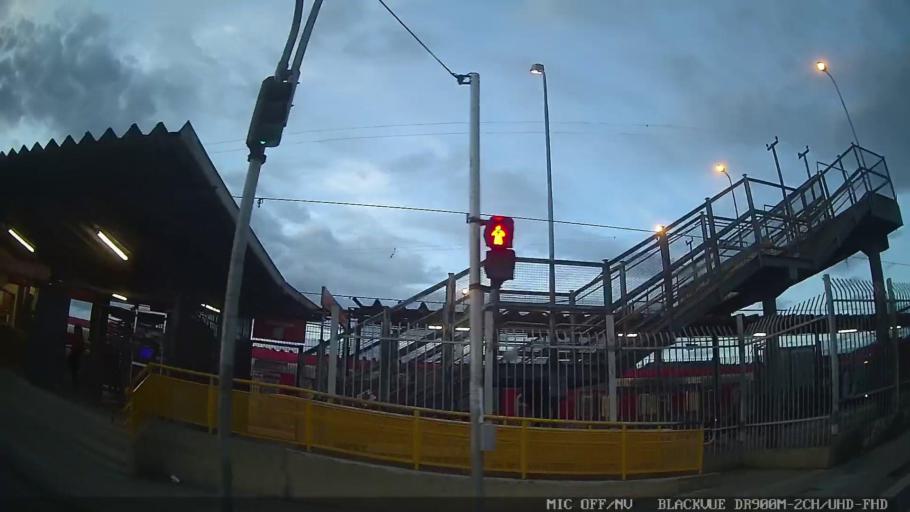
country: BR
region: Sao Paulo
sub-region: Mogi das Cruzes
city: Mogi das Cruzes
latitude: -23.5364
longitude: -46.2249
